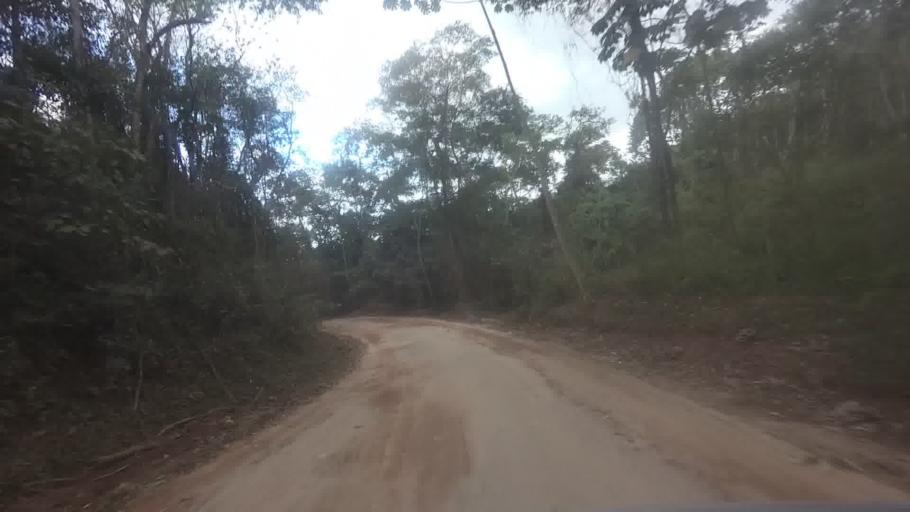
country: BR
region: Espirito Santo
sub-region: Mimoso Do Sul
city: Mimoso do Sul
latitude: -20.9445
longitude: -41.4020
